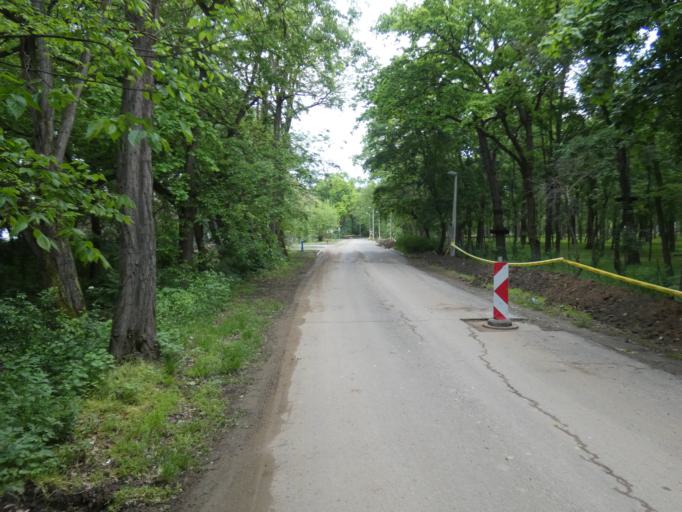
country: HU
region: Szabolcs-Szatmar-Bereg
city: Kotaj
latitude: 48.0070
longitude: 21.7212
